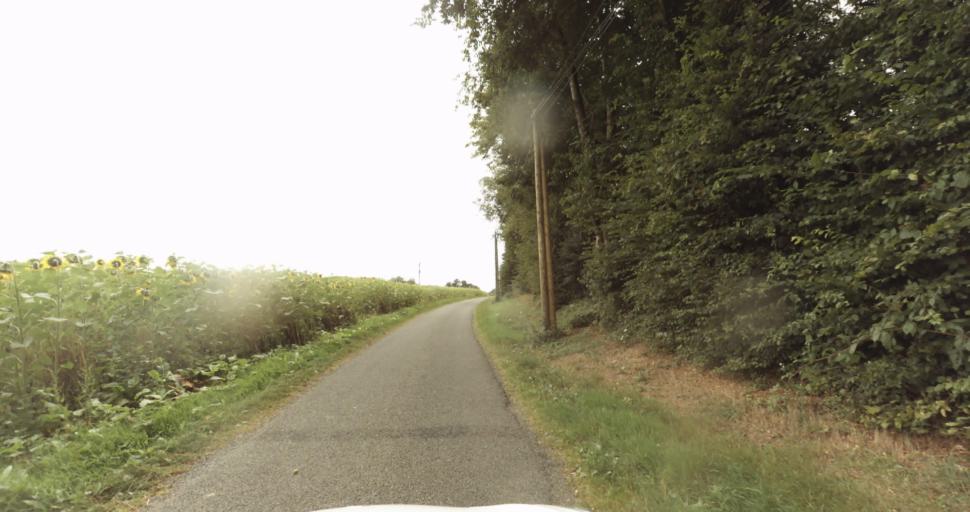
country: FR
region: Haute-Normandie
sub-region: Departement de l'Eure
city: Saint-Germain-sur-Avre
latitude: 48.8286
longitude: 1.2543
